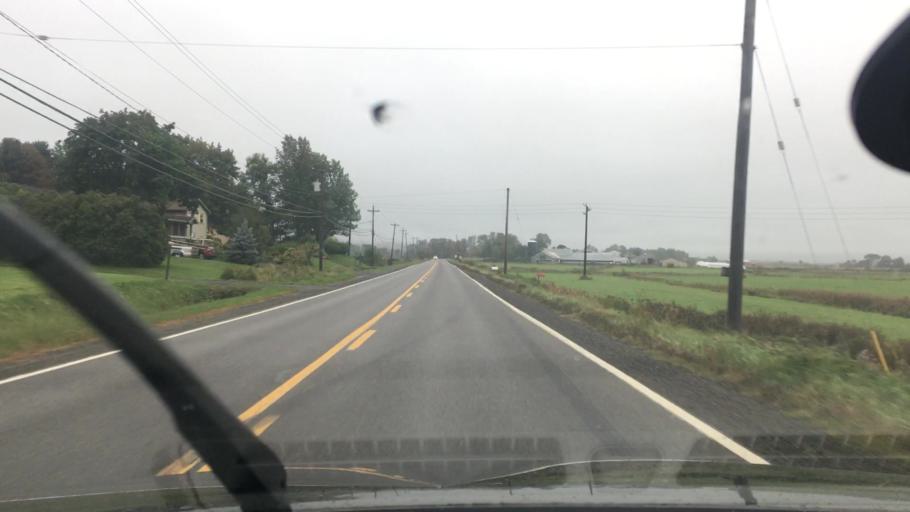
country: CA
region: Nova Scotia
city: Windsor
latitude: 44.9738
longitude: -64.1373
